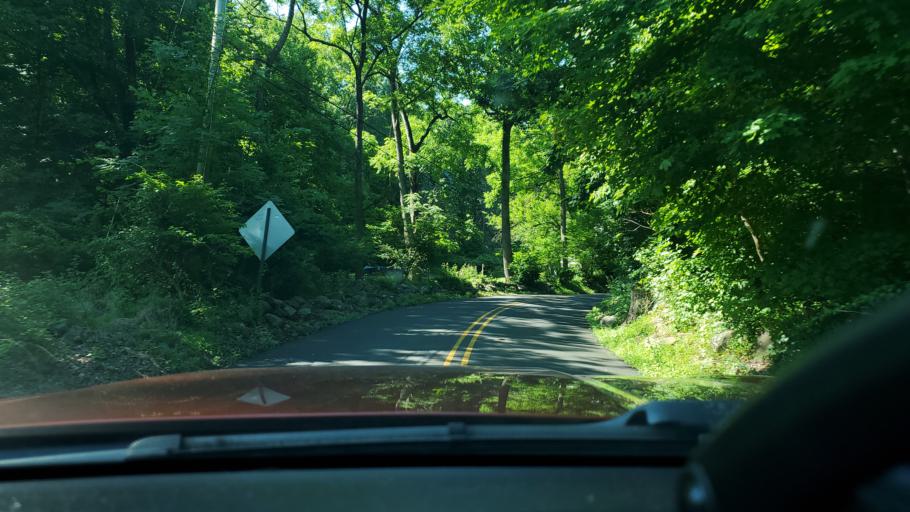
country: US
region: Pennsylvania
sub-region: Montgomery County
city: Red Hill
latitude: 40.3361
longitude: -75.5108
